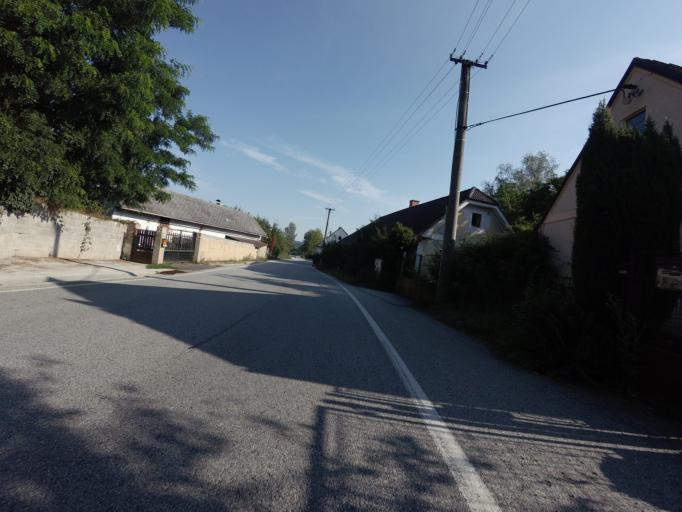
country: CZ
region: Jihocesky
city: Tyn nad Vltavou
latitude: 49.2406
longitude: 14.4200
